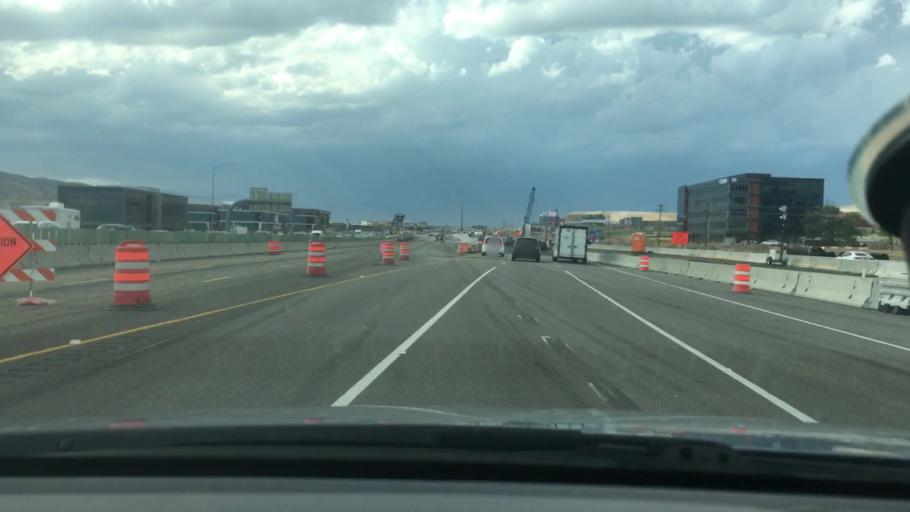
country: US
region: Utah
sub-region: Utah County
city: Lehi
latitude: 40.4172
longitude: -111.8743
